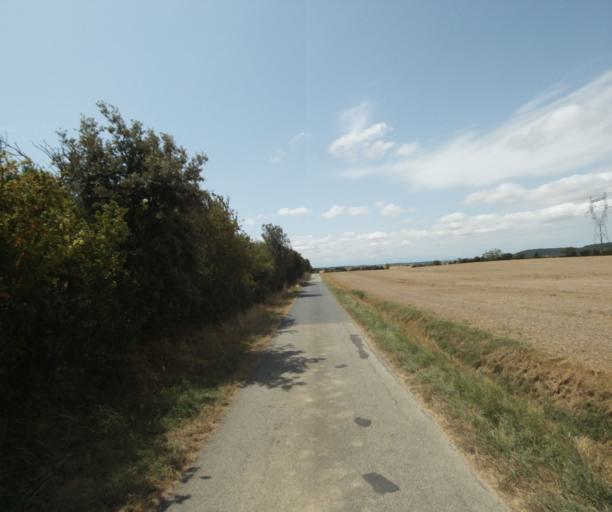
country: FR
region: Midi-Pyrenees
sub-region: Departement de la Haute-Garonne
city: Saint-Felix-Lauragais
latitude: 43.4316
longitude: 1.8815
